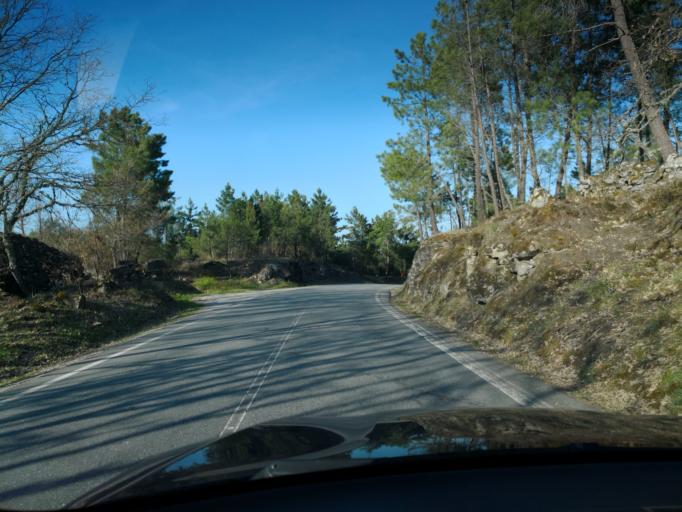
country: PT
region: Vila Real
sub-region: Sabrosa
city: Sabrosa
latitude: 41.3532
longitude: -7.6099
